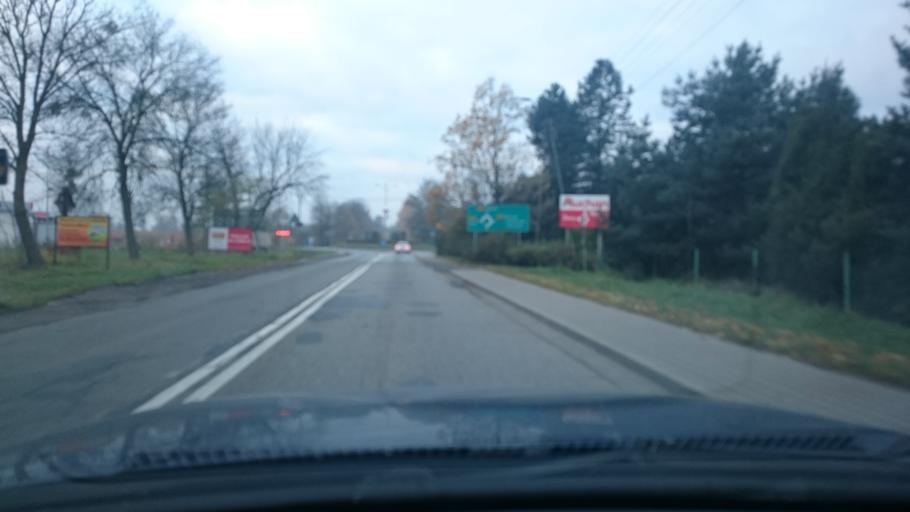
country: PL
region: Silesian Voivodeship
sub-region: Powiat rybnicki
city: Stanowice
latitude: 50.1303
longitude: 18.6749
